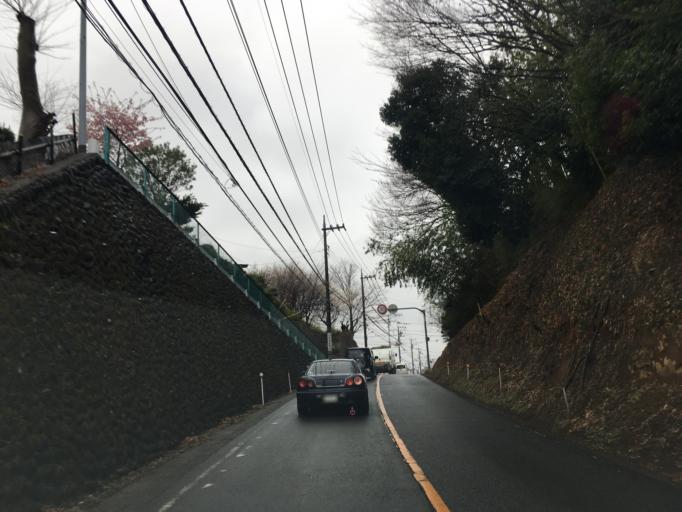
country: JP
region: Tokyo
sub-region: Machida-shi
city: Machida
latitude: 35.5734
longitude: 139.4289
